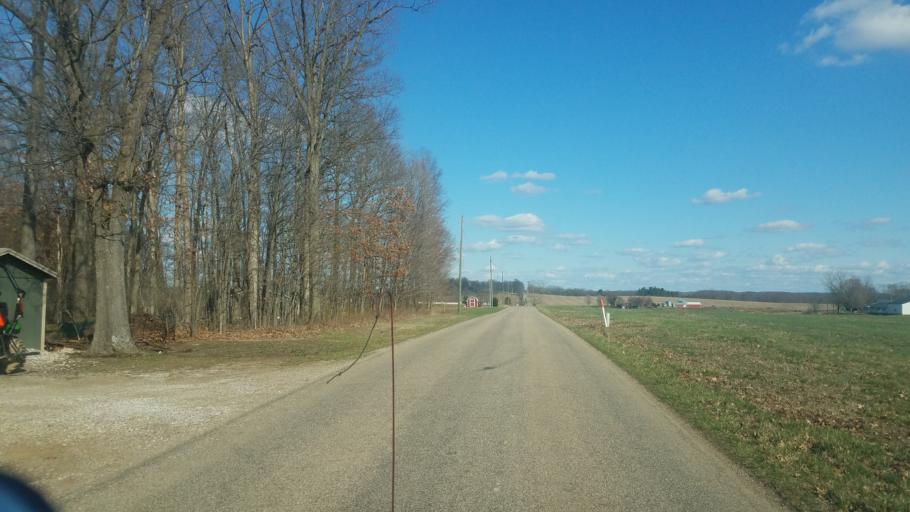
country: US
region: Ohio
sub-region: Licking County
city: Utica
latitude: 40.2616
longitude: -82.3120
